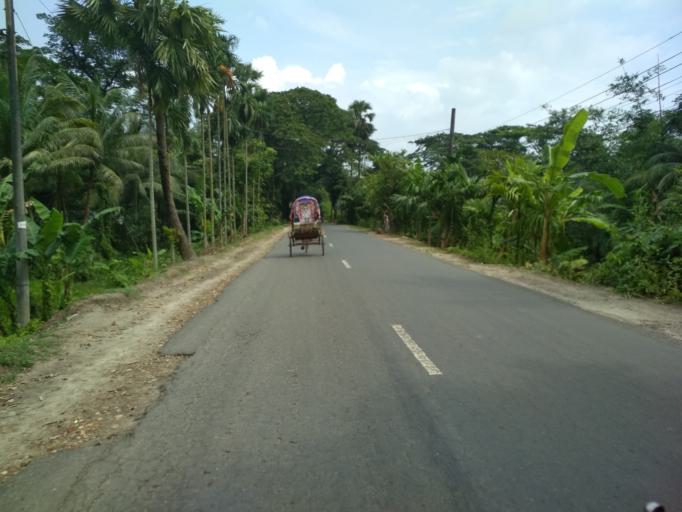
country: BD
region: Chittagong
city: Lakshmipur
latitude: 22.9577
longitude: 90.8092
